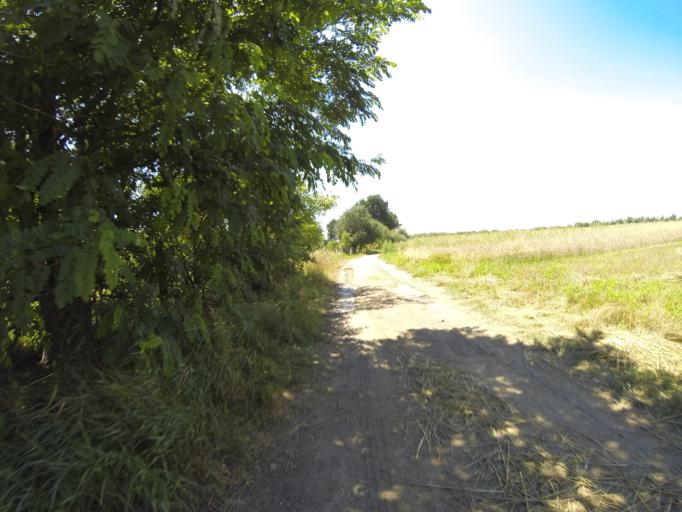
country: RO
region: Brasov
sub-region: Comuna Sinca Veche
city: Sinca Veche
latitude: 45.7671
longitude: 25.1662
